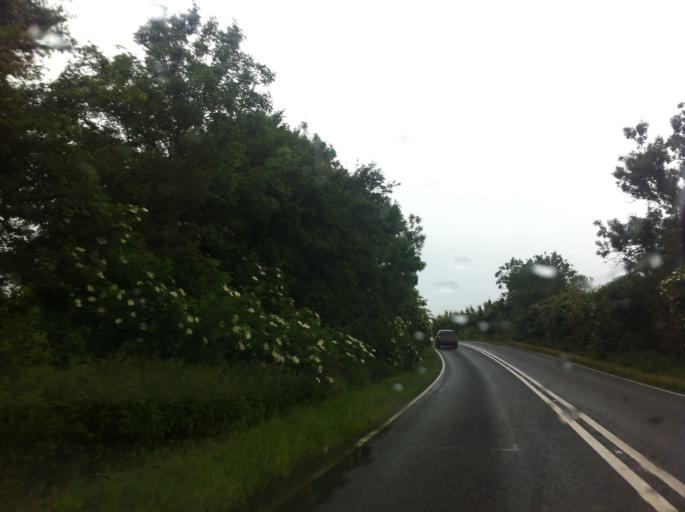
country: GB
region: England
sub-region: Northamptonshire
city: Irchester
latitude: 52.2677
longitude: -0.6769
